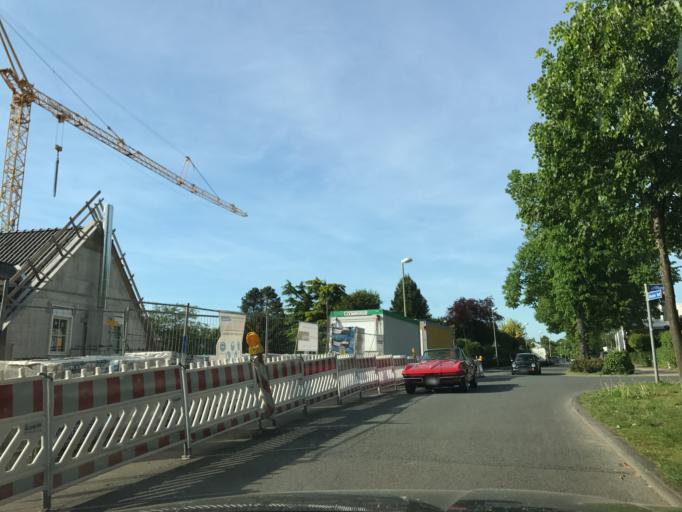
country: DE
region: North Rhine-Westphalia
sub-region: Regierungsbezirk Dusseldorf
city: Essen
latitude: 51.4075
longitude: 6.9760
